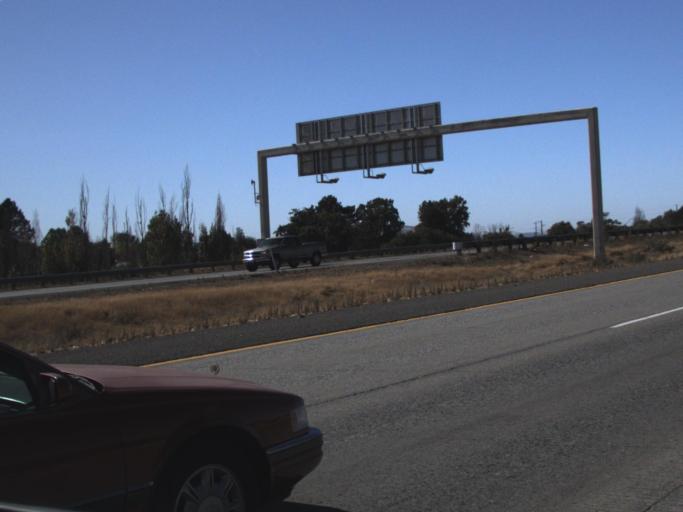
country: US
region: Washington
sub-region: Franklin County
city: West Pasco
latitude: 46.2564
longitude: -119.1521
